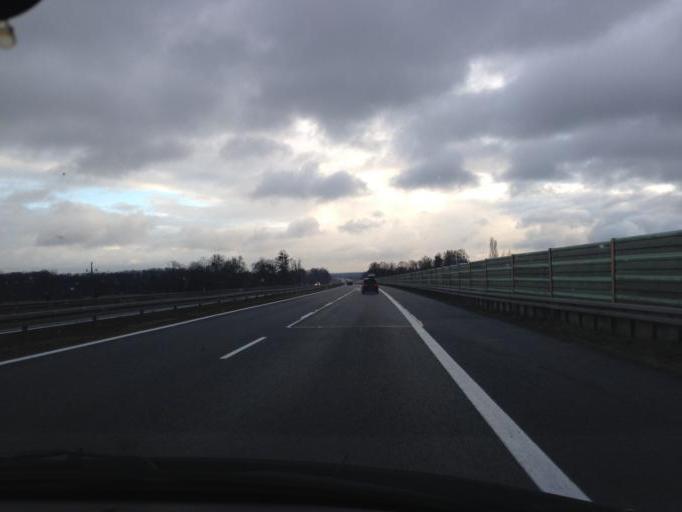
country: PL
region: Opole Voivodeship
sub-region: Powiat strzelecki
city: Ujazd
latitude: 50.4155
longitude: 18.4053
